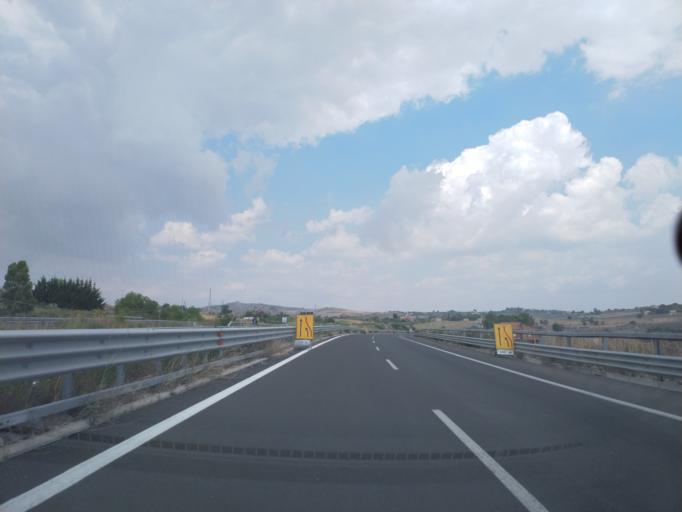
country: IT
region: Sicily
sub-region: Agrigento
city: Racalmuto
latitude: 37.3895
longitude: 13.7460
